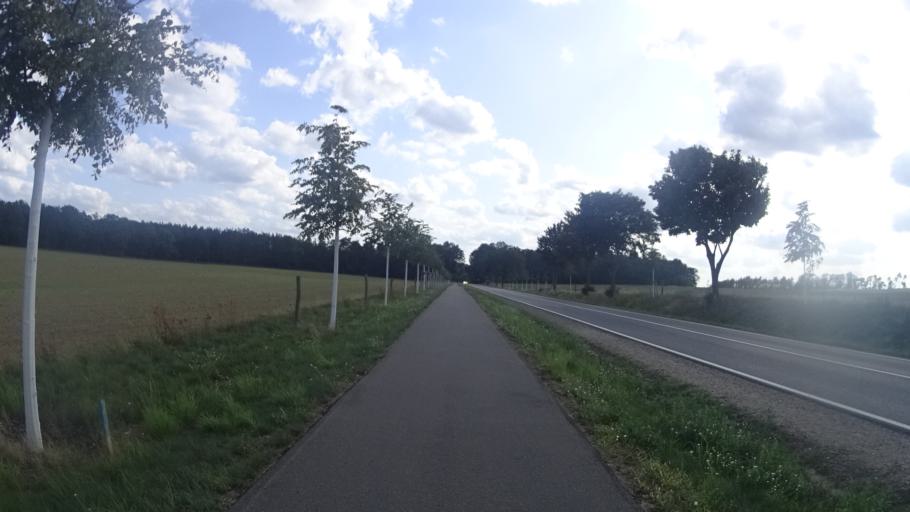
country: DE
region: Brandenburg
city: Rhinow
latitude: 52.6929
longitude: 12.3658
